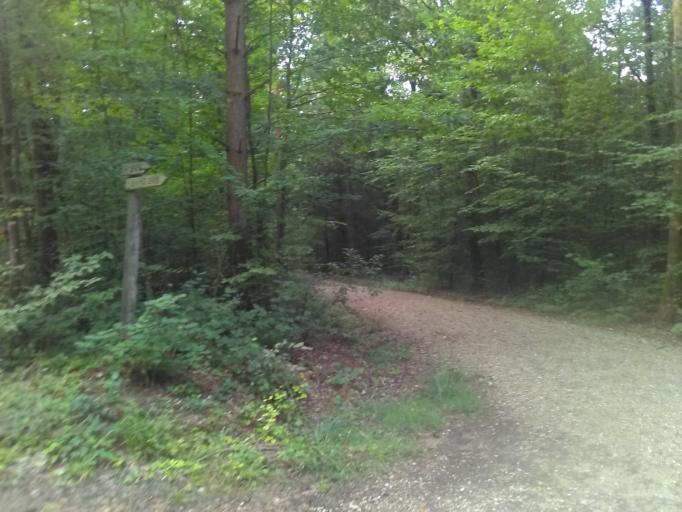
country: DE
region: Bavaria
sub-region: Upper Franconia
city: Pettstadt
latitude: 49.8496
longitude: 10.9114
